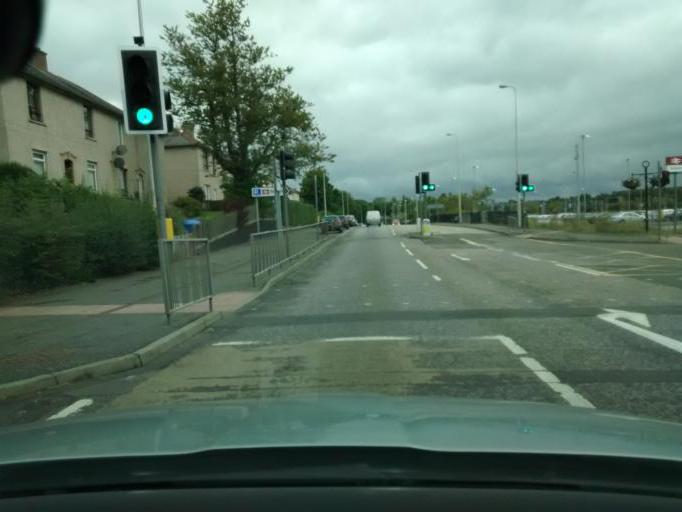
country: GB
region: Scotland
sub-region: West Lothian
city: Bathgate
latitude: 55.8978
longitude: -3.6356
